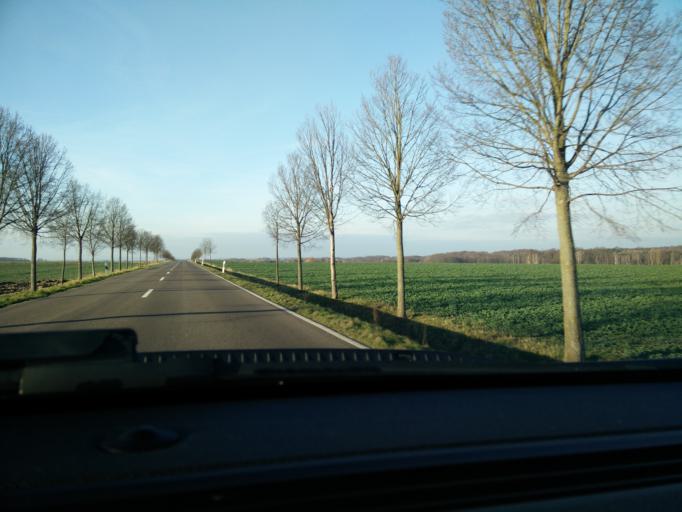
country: DE
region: Saxony
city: Bad Lausick
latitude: 51.1111
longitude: 12.6852
